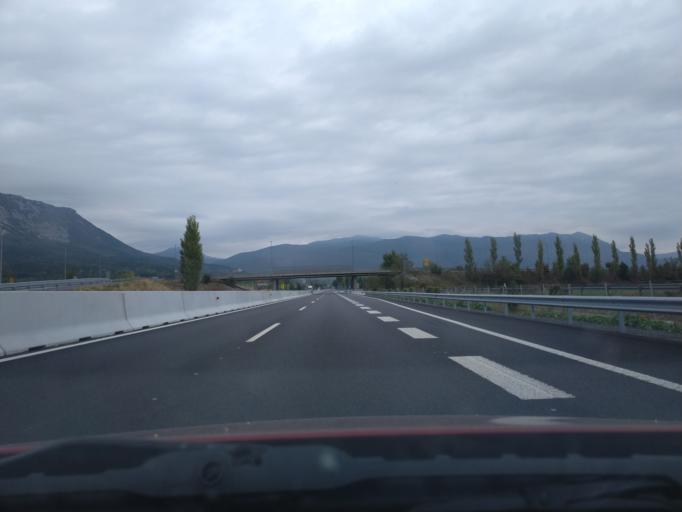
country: SI
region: Ajdovscina
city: Ajdovscina
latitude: 45.8806
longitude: 13.8998
